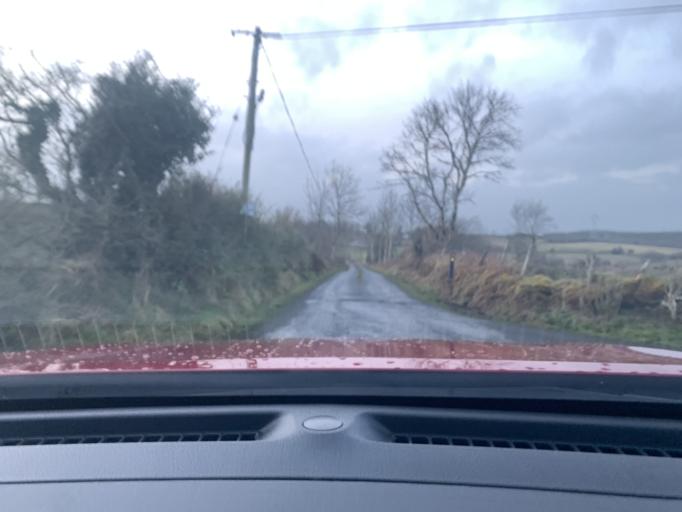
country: IE
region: Connaught
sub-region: Sligo
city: Ballymote
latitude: 53.9920
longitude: -8.4555
